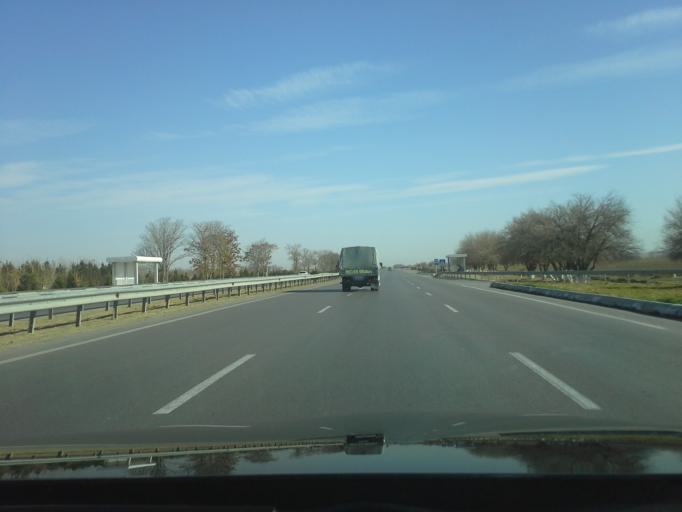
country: TM
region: Ahal
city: Annau
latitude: 37.9034
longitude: 58.5519
